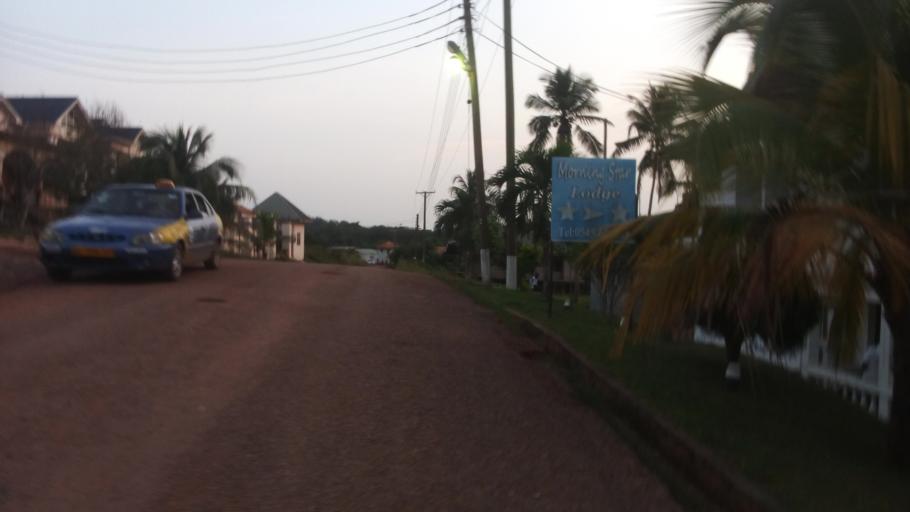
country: GH
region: Western
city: Tarkwa
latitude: 5.3061
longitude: -2.0014
